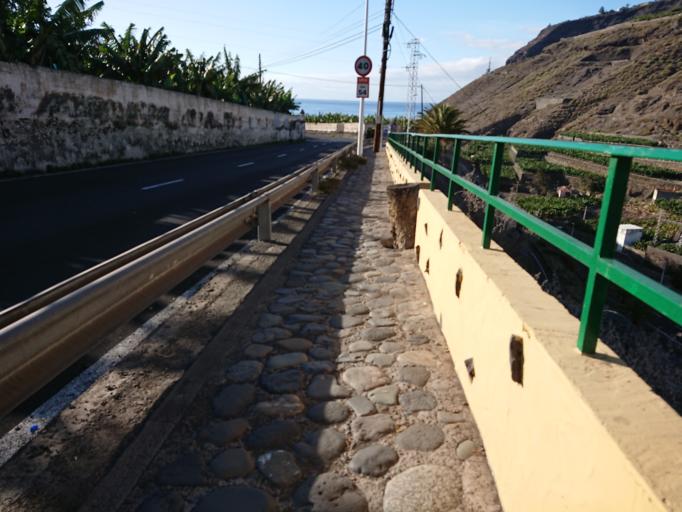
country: ES
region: Canary Islands
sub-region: Provincia de Santa Cruz de Tenerife
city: Tazacorte
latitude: 28.6461
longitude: -17.9377
